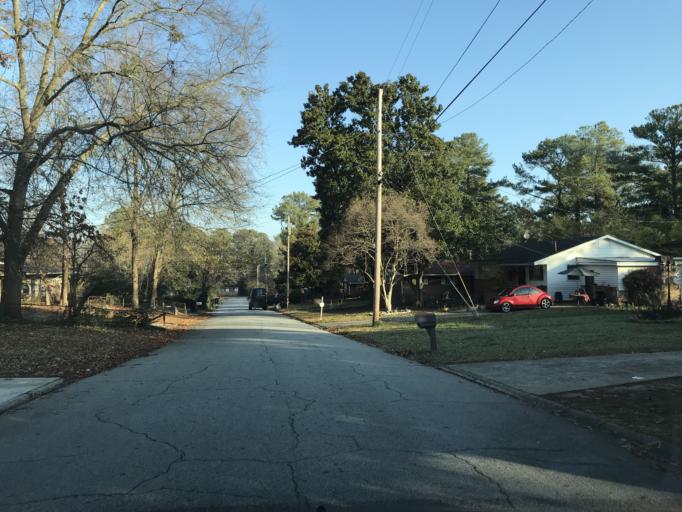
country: US
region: Georgia
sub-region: Fulton County
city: College Park
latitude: 33.6126
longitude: -84.4347
